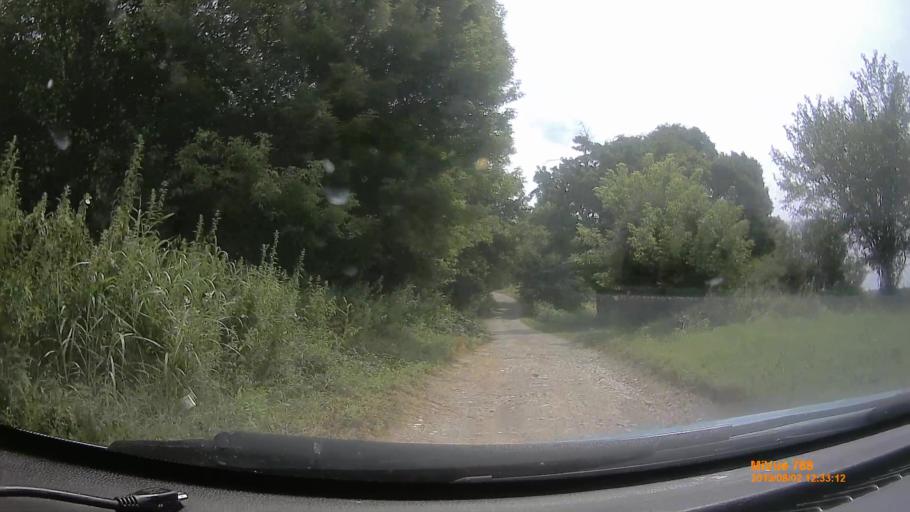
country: HU
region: Baranya
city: Buekkoesd
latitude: 46.1012
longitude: 17.9422
